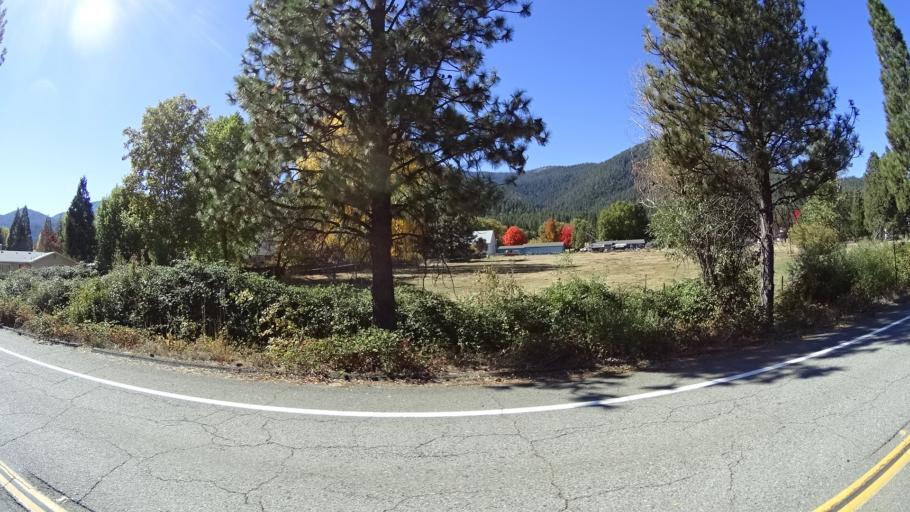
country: US
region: California
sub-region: Siskiyou County
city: Yreka
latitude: 41.4599
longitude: -122.8958
